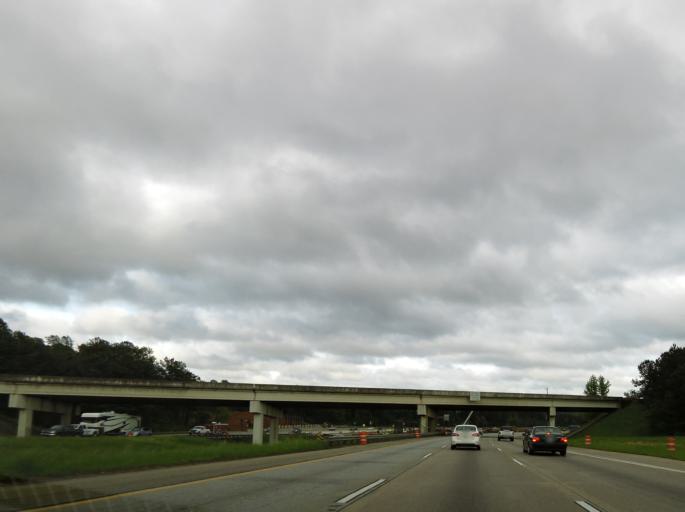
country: US
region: Georgia
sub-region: Henry County
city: Stockbridge
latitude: 33.5439
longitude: -84.2716
